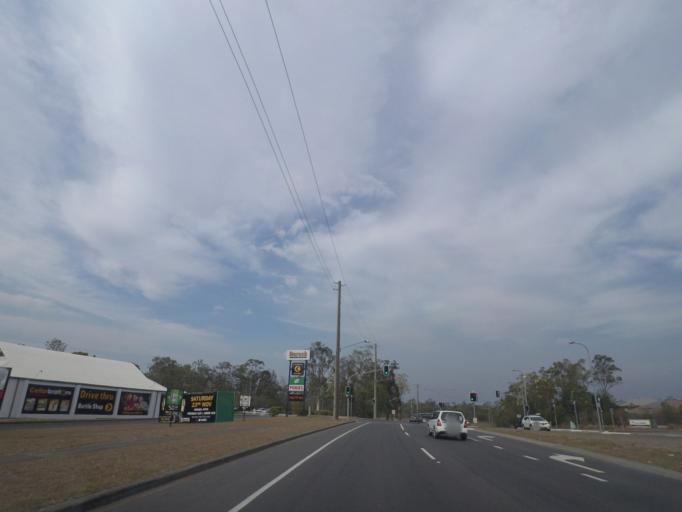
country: AU
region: Queensland
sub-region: Brisbane
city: Inala
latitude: -27.5938
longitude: 152.9915
